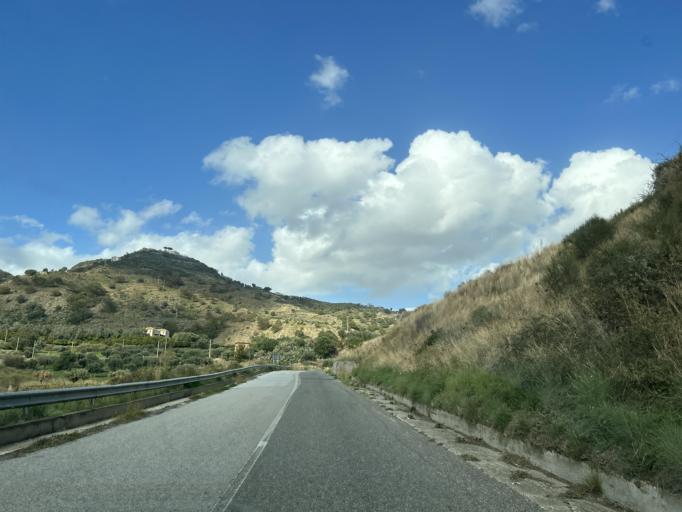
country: IT
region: Calabria
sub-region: Provincia di Catanzaro
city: Gasperina
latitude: 38.7248
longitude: 16.5189
